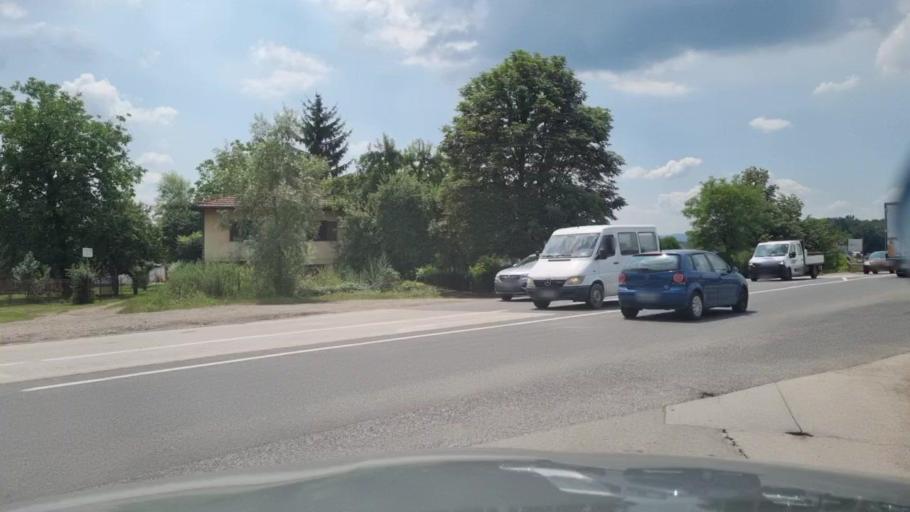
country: BA
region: Federation of Bosnia and Herzegovina
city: Kiseljak
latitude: 44.5204
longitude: 18.5916
